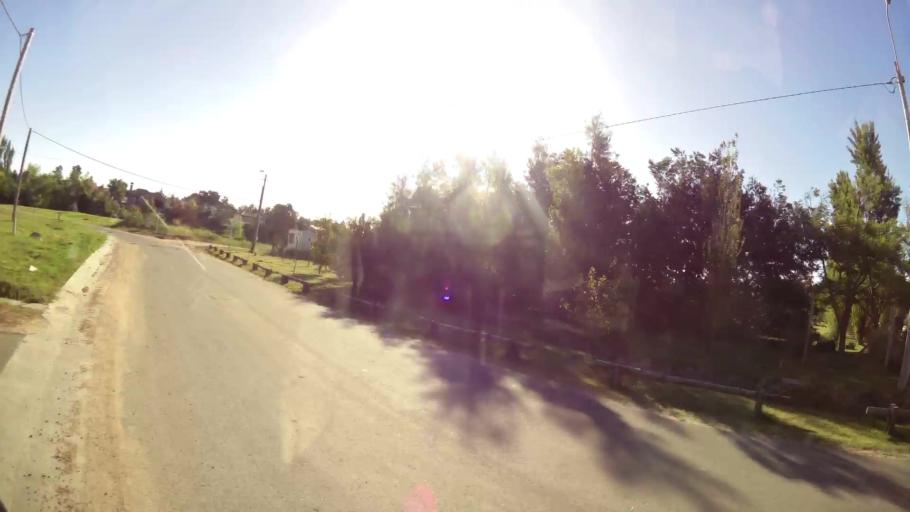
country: UY
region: Canelones
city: Paso de Carrasco
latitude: -34.8682
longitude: -56.0413
